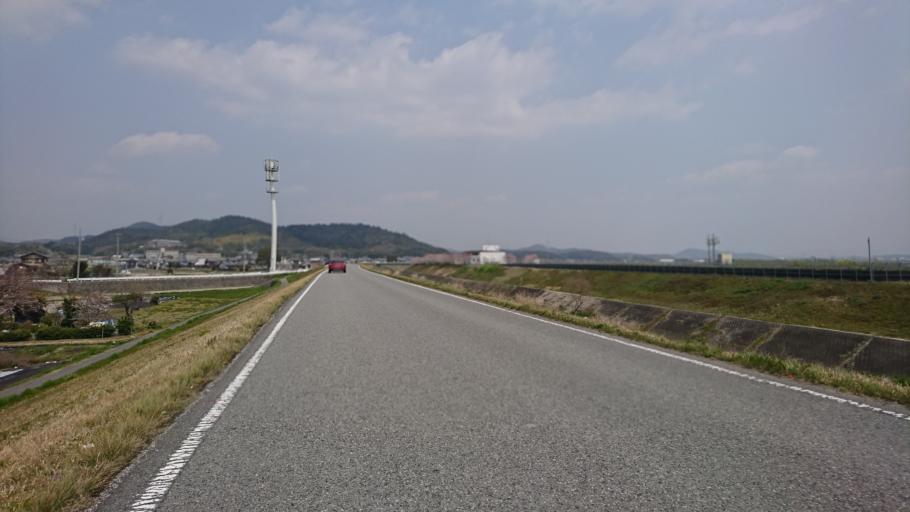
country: JP
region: Hyogo
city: Kakogawacho-honmachi
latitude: 34.7955
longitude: 134.8674
